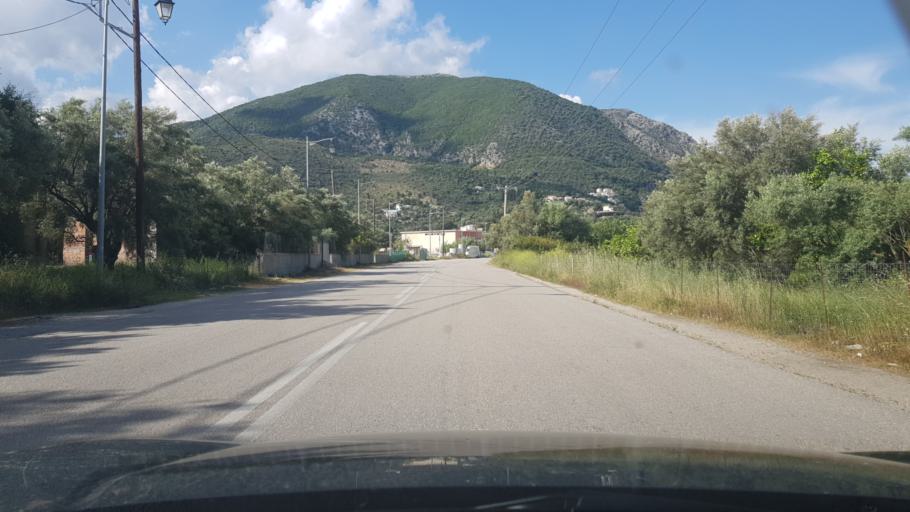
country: GR
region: Ionian Islands
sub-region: Lefkada
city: Nidri
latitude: 38.7074
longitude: 20.7042
